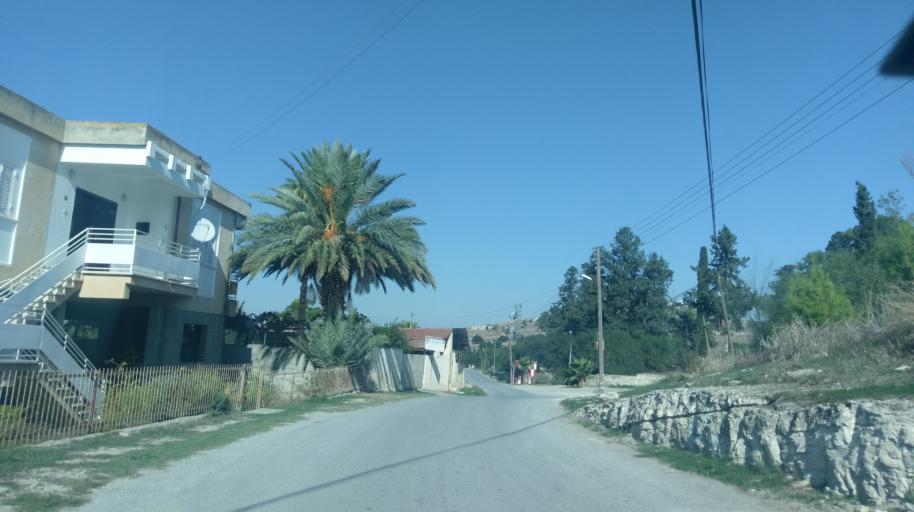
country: CY
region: Lefkosia
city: Lympia
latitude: 35.0139
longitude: 33.4648
